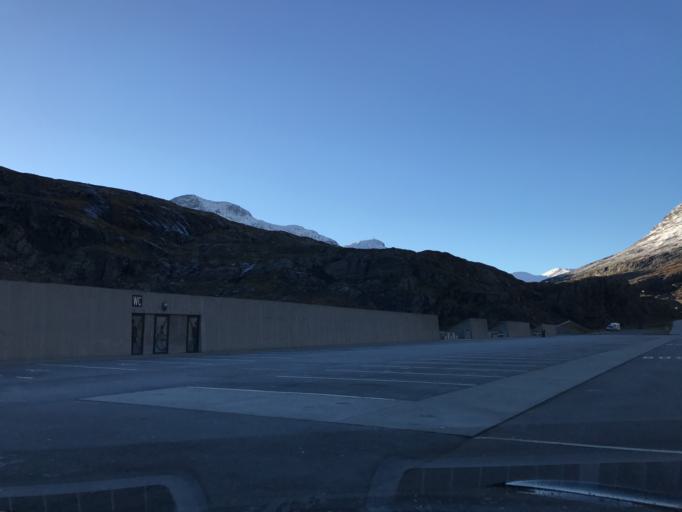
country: NO
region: More og Romsdal
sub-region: Rauma
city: Andalsnes
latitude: 62.4537
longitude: 7.6638
